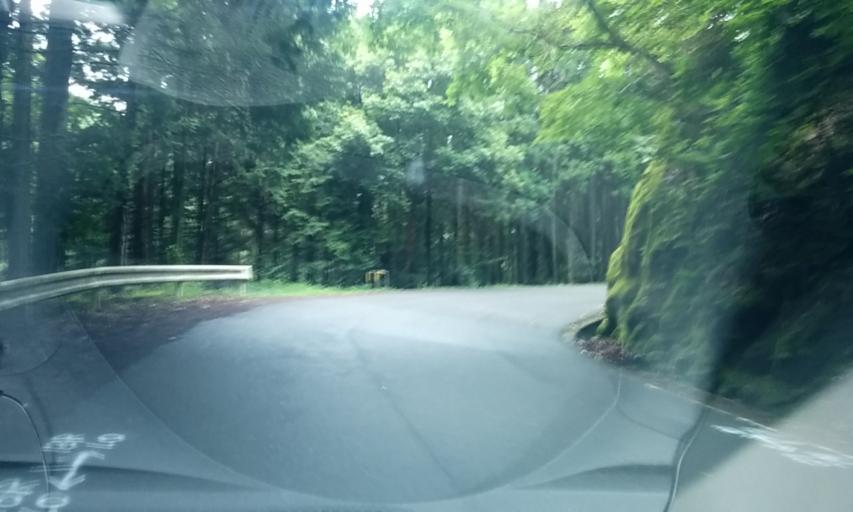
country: JP
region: Kyoto
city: Kameoka
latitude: 35.0551
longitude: 135.4263
